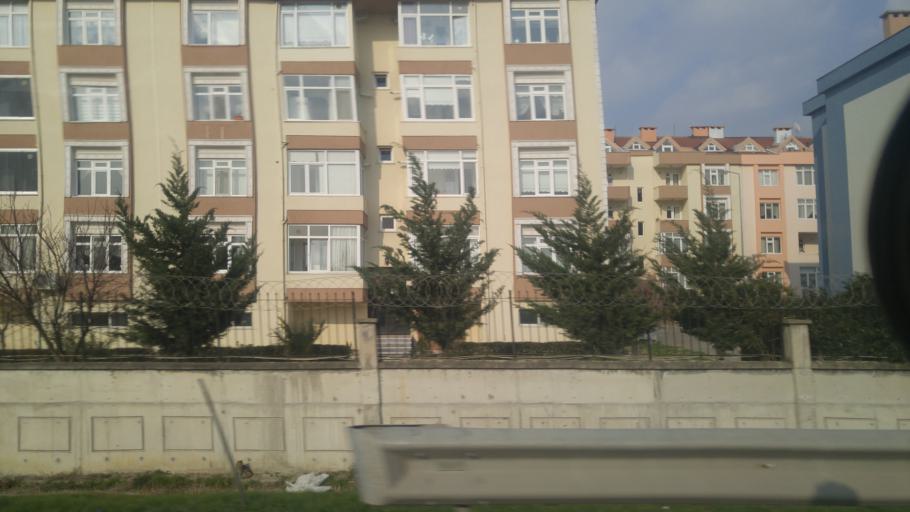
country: TR
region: Istanbul
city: Selimpasa
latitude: 41.0526
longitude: 28.3828
